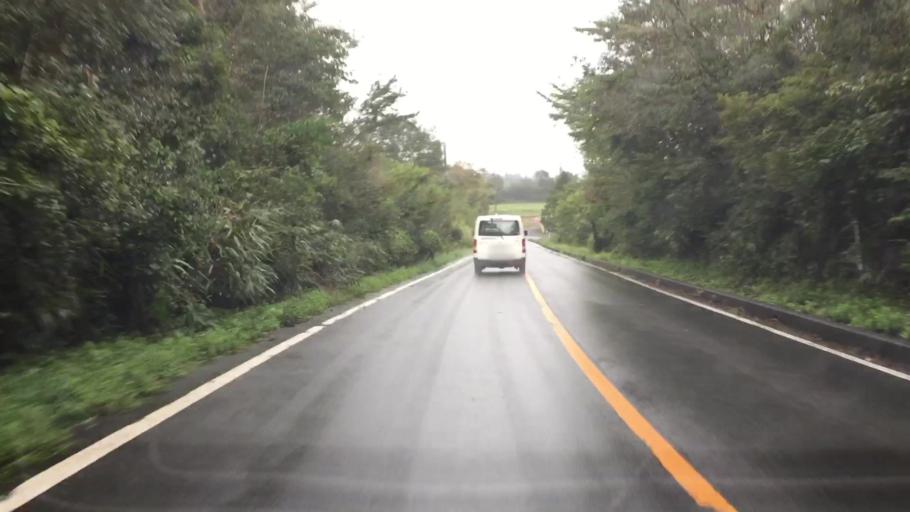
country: JP
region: Yamanashi
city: Fujikawaguchiko
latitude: 35.4215
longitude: 138.6245
